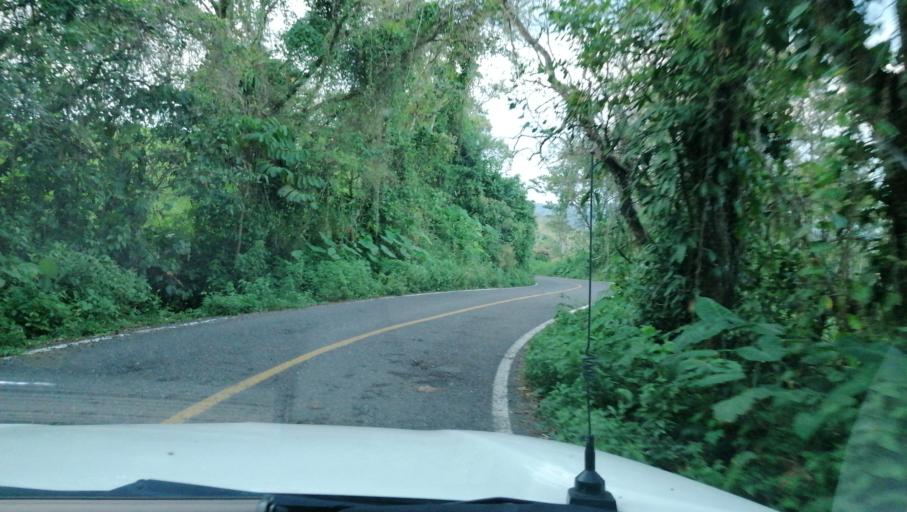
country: MX
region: Chiapas
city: Pichucalco
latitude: 17.5182
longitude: -93.1560
